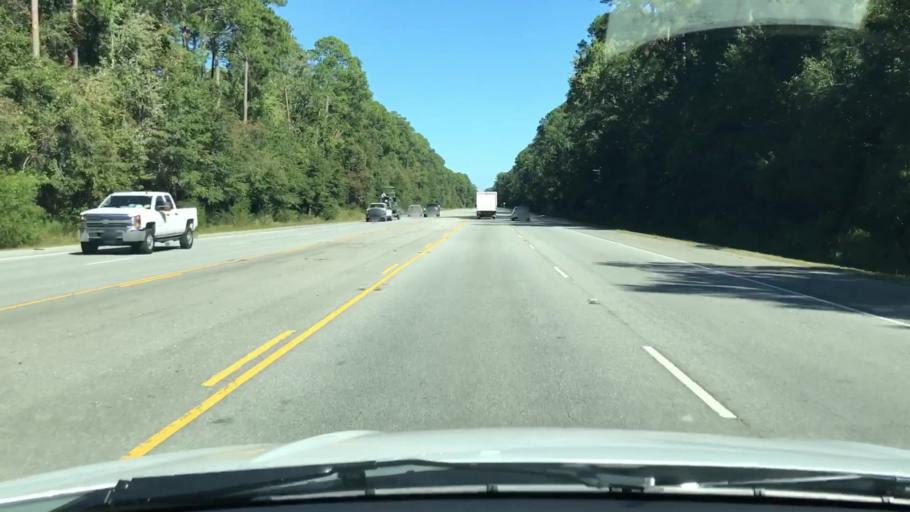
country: US
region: South Carolina
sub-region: Beaufort County
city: Burton
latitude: 32.4190
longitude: -80.7426
